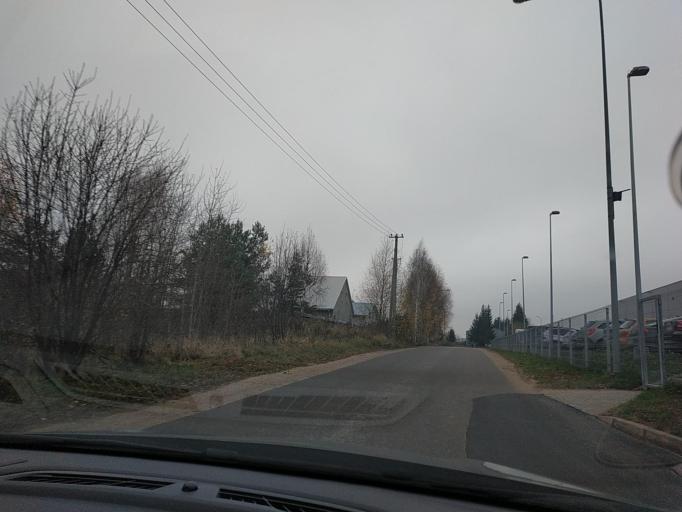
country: LT
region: Vilnius County
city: Rasos
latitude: 54.6414
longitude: 25.3343
